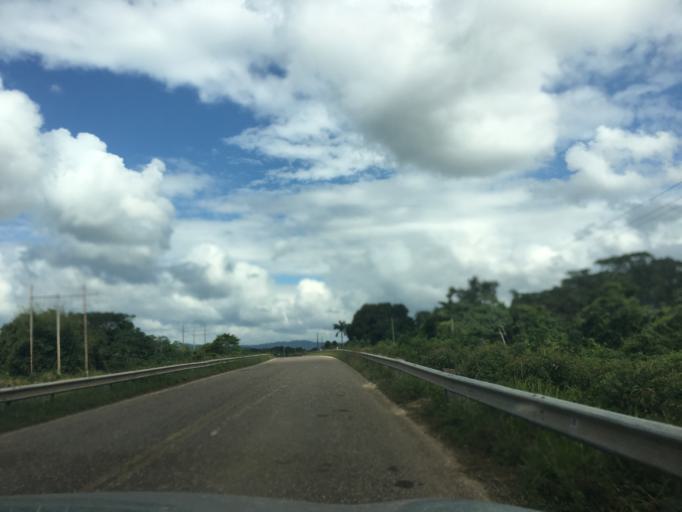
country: BZ
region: Stann Creek
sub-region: Dangriga
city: Dangriga
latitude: 16.8608
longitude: -88.3469
